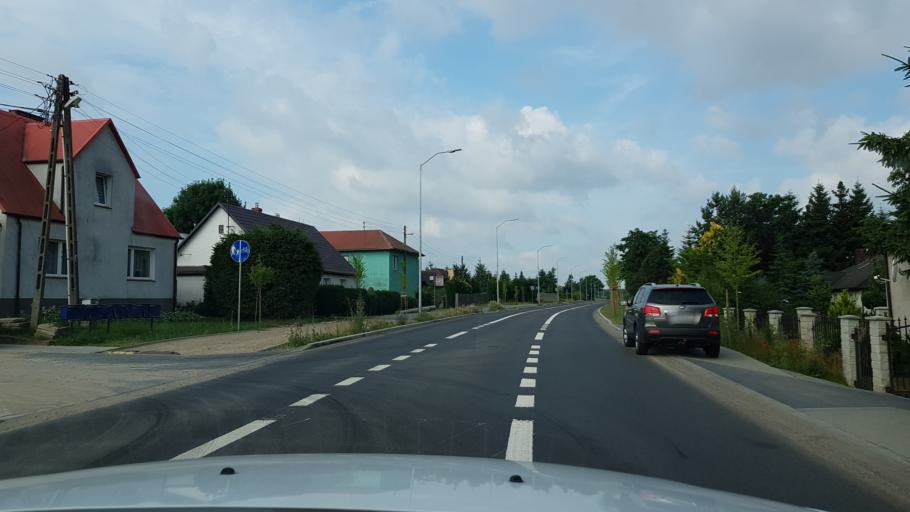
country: PL
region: West Pomeranian Voivodeship
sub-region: Powiat gryfinski
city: Gryfino
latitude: 53.2581
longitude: 14.5703
